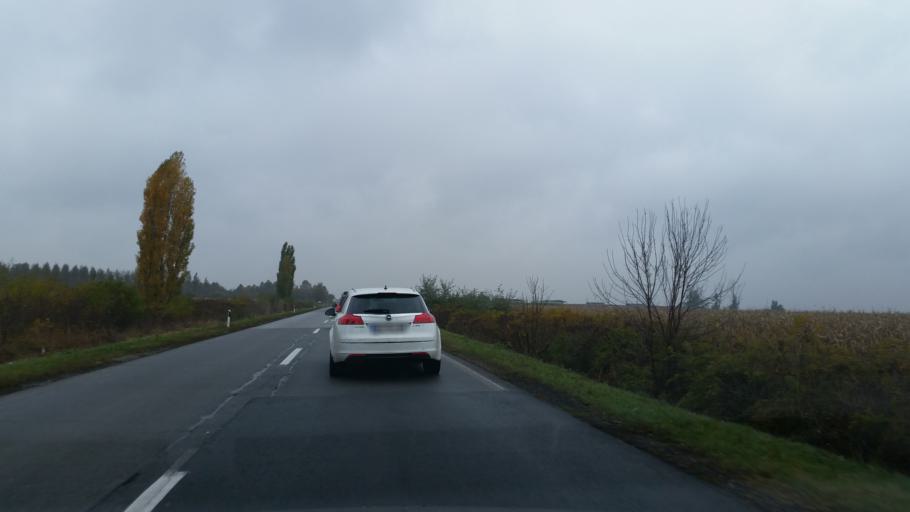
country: RS
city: Sefkerin
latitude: 44.9423
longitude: 20.4346
